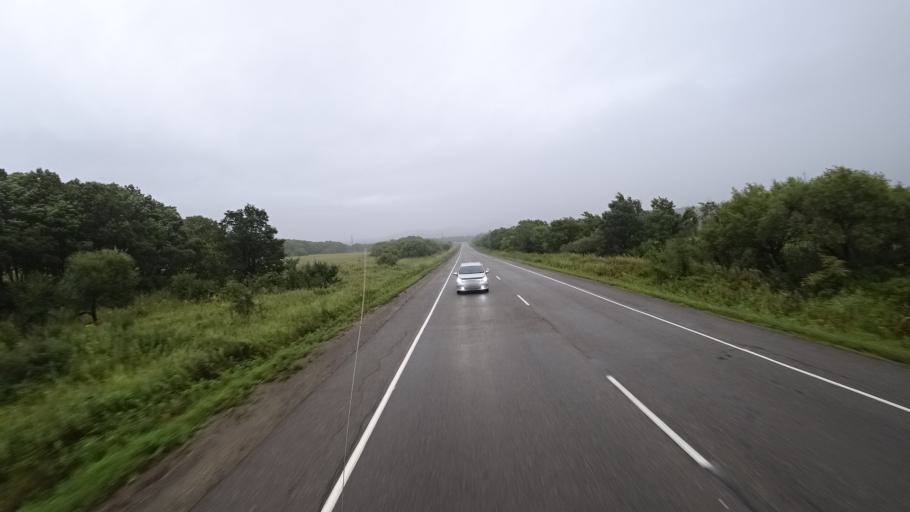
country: RU
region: Primorskiy
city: Monastyrishche
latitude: 44.2749
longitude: 132.4778
